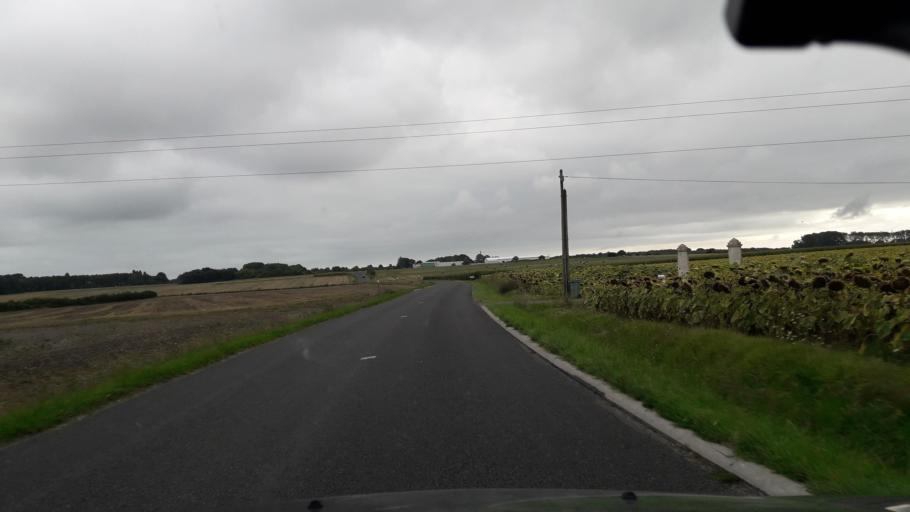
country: FR
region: Poitou-Charentes
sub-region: Departement de la Charente-Maritime
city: Arvert
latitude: 45.7314
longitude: -1.1323
